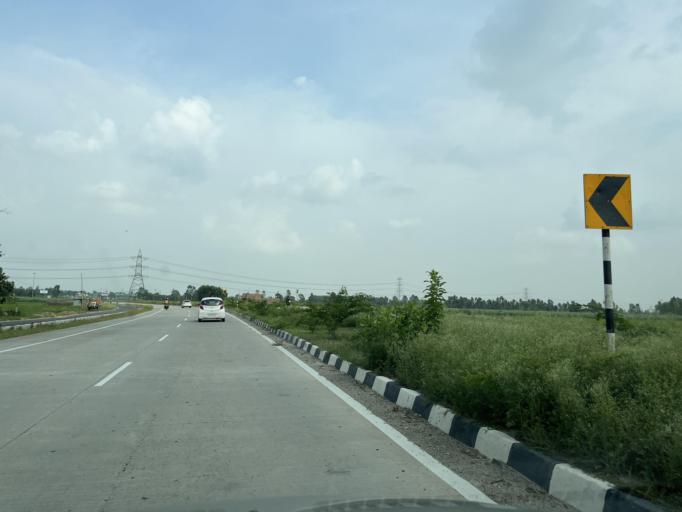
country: IN
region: Uttarakhand
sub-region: Udham Singh Nagar
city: Bazpur
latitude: 29.1496
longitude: 79.0778
